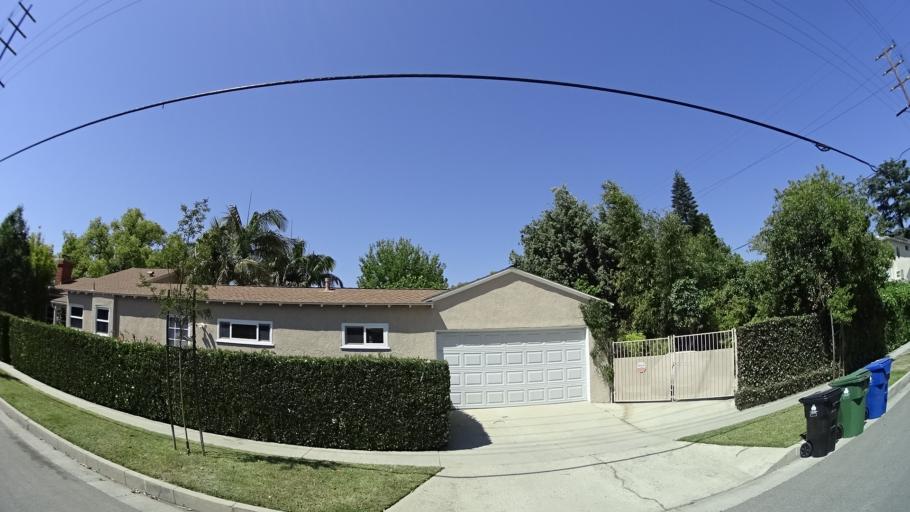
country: US
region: California
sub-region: Los Angeles County
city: North Hollywood
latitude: 34.1758
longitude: -118.3862
